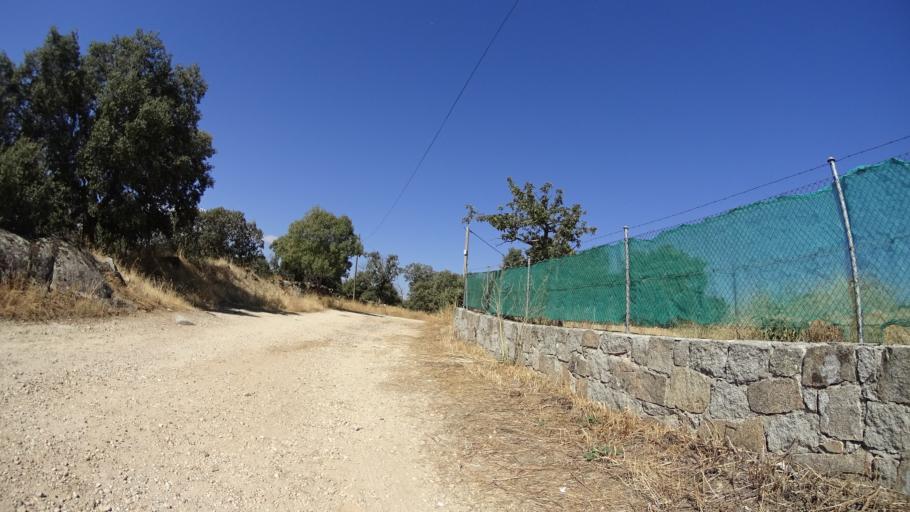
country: ES
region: Madrid
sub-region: Provincia de Madrid
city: Collado-Villalba
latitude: 40.6124
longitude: -4.0034
